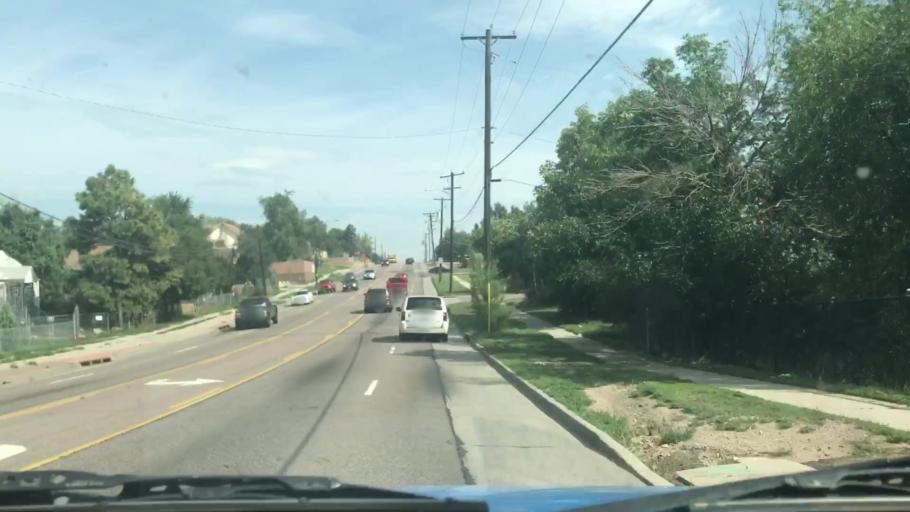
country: US
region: Colorado
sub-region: Jefferson County
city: Lakewood
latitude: 39.7044
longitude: -105.0532
